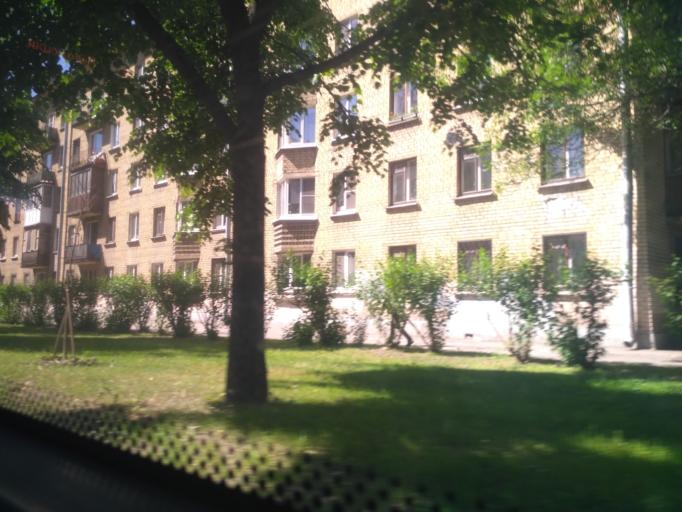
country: RU
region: Leningrad
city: Kalininskiy
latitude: 59.9613
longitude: 30.4224
